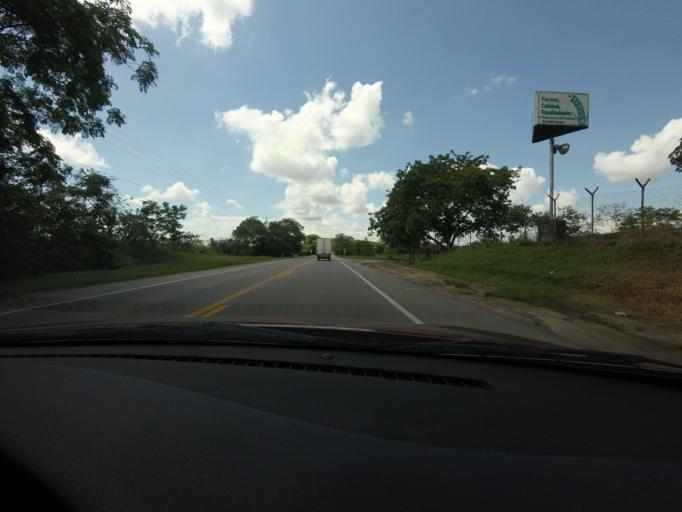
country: CO
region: Tolima
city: Saldana
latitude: 3.9517
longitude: -75.0067
